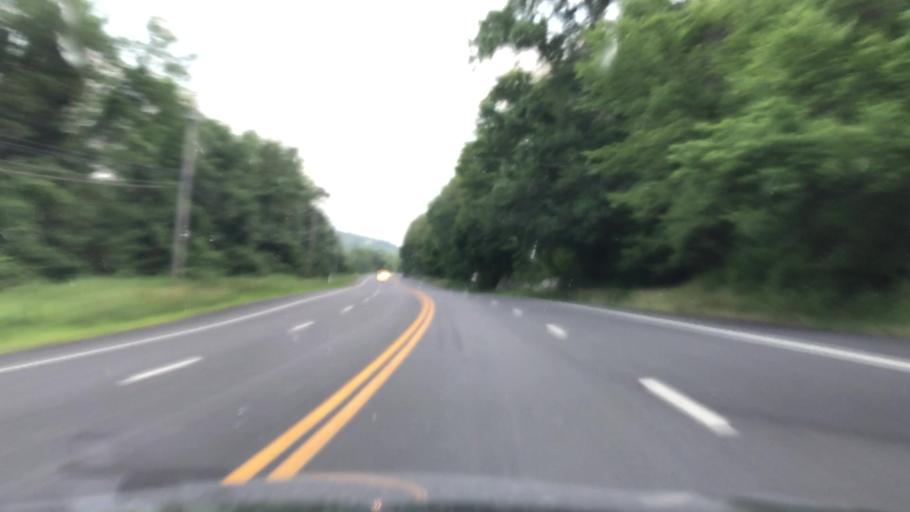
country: US
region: New York
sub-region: Orange County
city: Harriman
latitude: 41.2367
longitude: -74.1786
